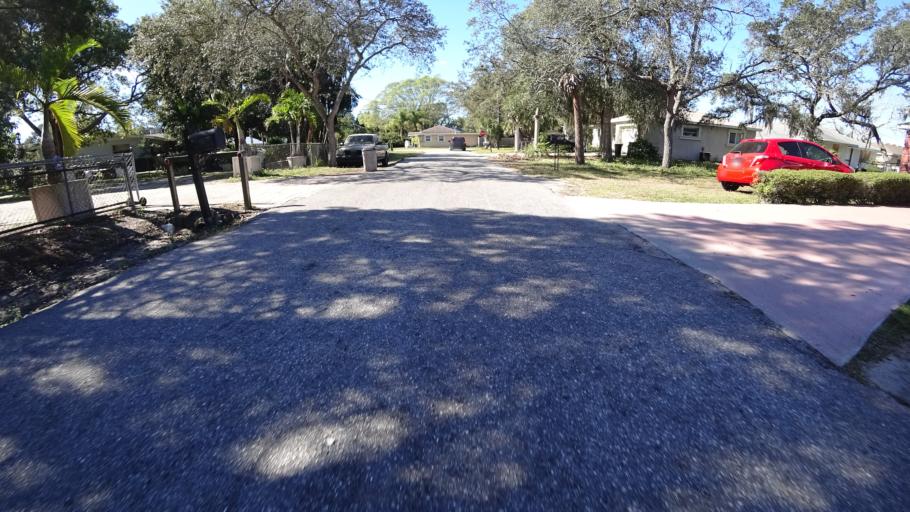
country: US
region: Florida
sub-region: Manatee County
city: West Samoset
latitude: 27.4789
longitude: -82.5583
